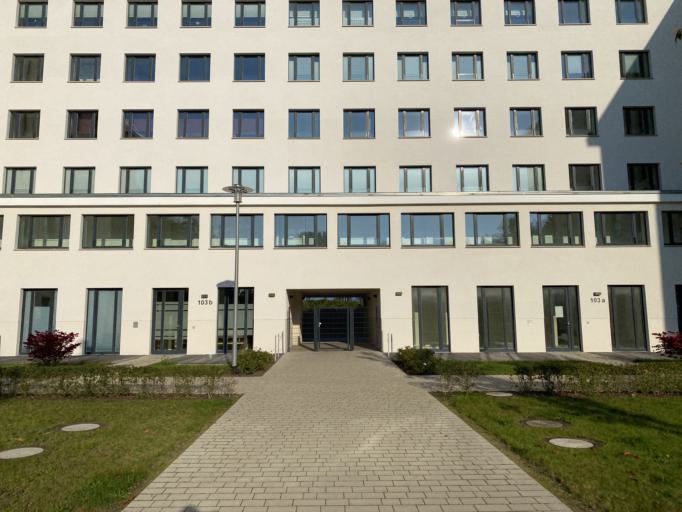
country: DE
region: Mecklenburg-Vorpommern
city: Ostseebad Binz
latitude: 54.4283
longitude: 13.5823
